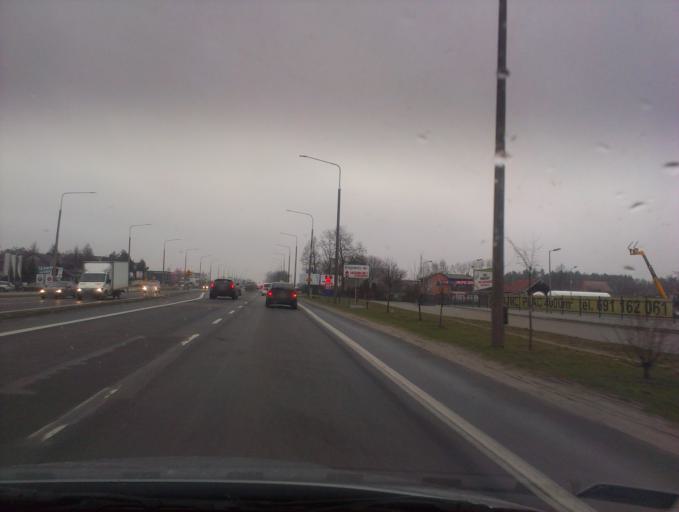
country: PL
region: Masovian Voivodeship
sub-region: Radom
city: Radom
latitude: 51.4459
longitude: 21.1445
